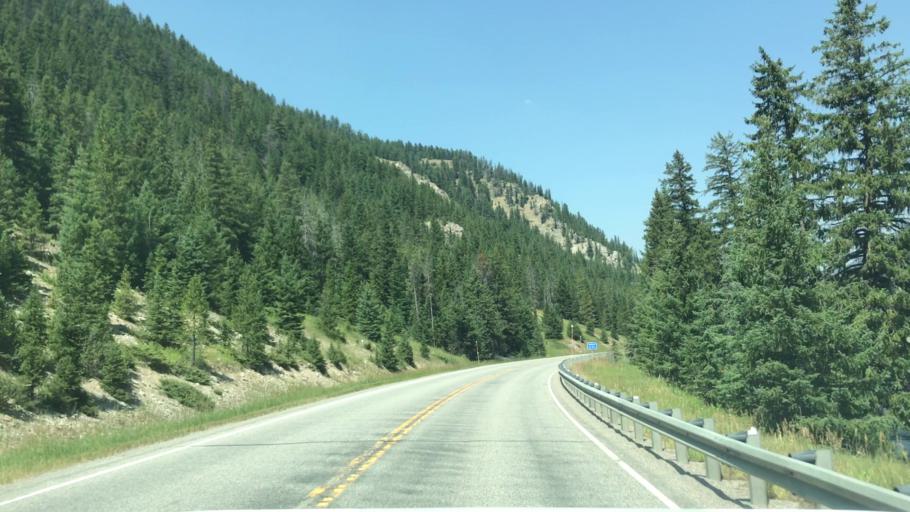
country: US
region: Montana
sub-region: Gallatin County
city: Big Sky
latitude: 45.0784
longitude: -111.2071
